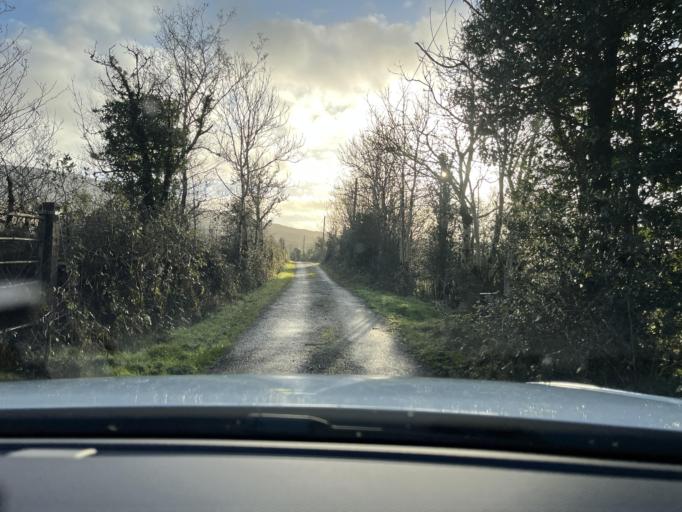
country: IE
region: Connaught
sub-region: County Leitrim
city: Manorhamilton
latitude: 54.2065
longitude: -7.9718
